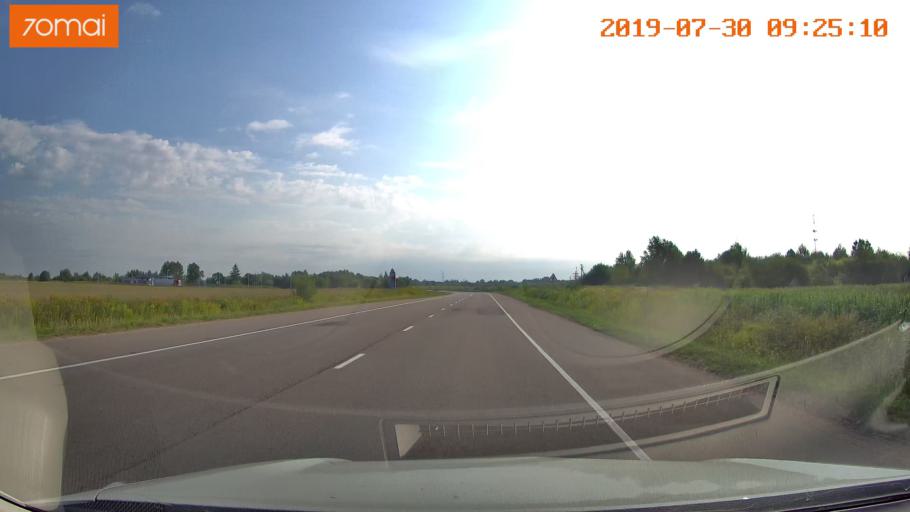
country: LT
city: Kybartai
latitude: 54.6370
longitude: 22.7086
